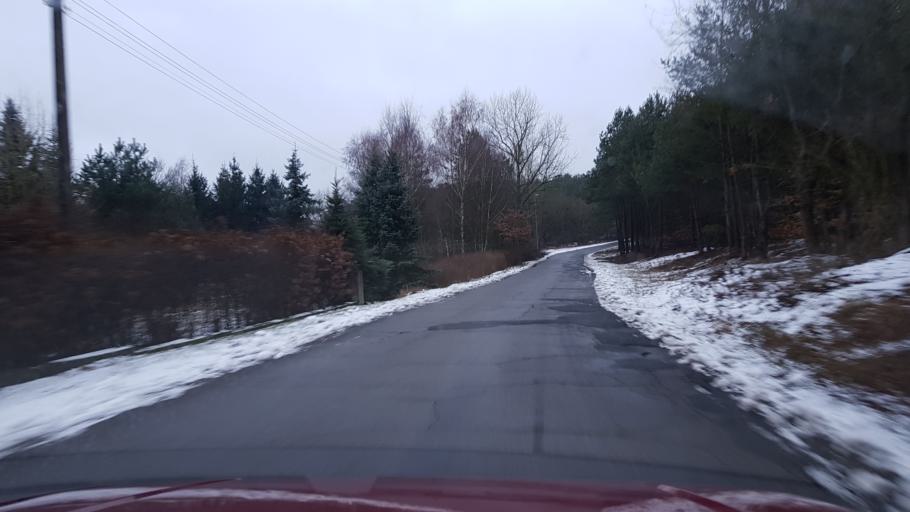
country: PL
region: West Pomeranian Voivodeship
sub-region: Powiat goleniowski
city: Mosty
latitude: 53.5016
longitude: 14.9029
